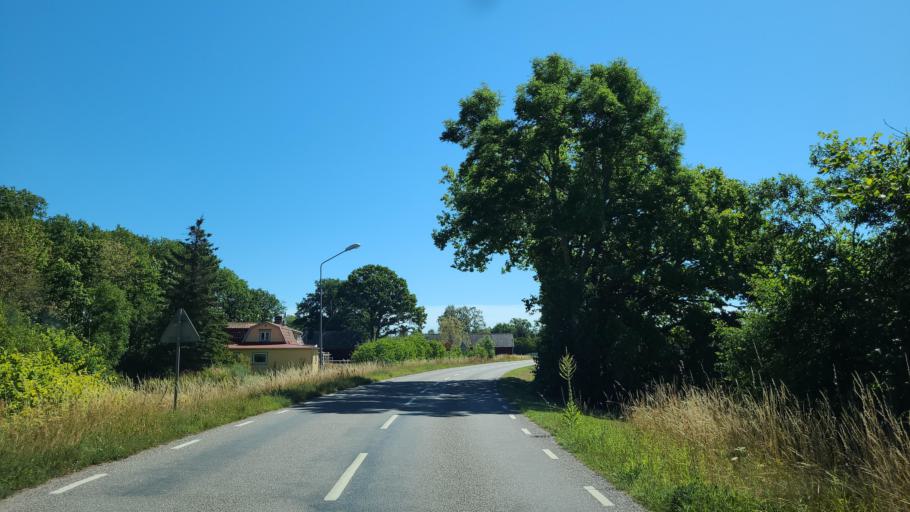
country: SE
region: Kalmar
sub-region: Borgholms Kommun
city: Borgholm
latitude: 56.7741
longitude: 16.5766
